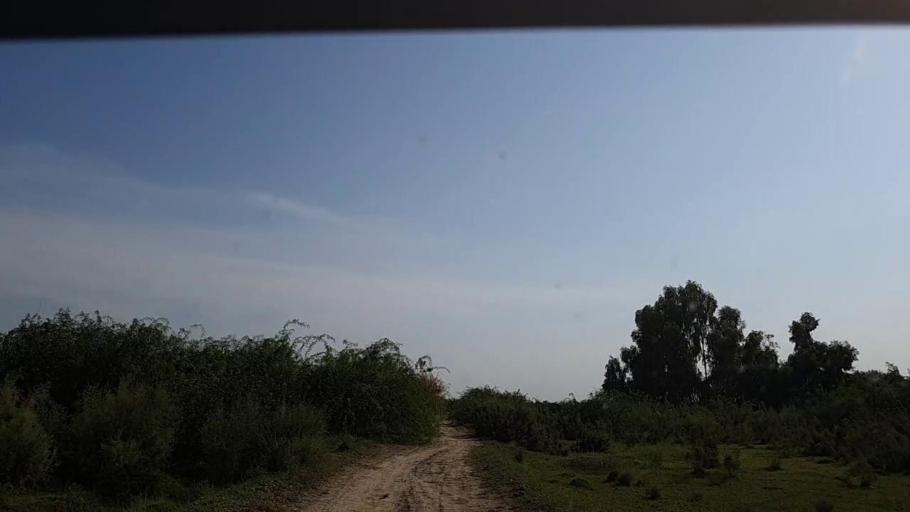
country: PK
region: Sindh
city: Adilpur
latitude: 27.9032
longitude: 69.2325
